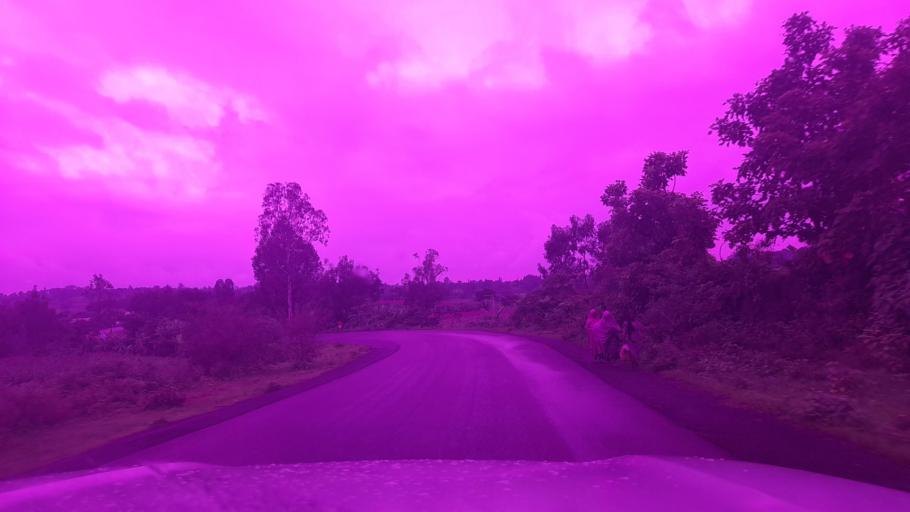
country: ET
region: Oromiya
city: Jima
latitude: 7.8264
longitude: 37.3455
